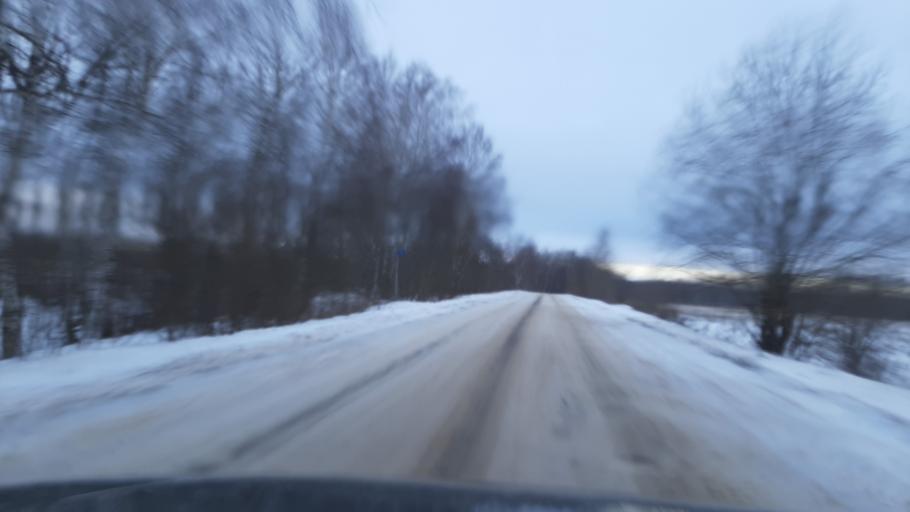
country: RU
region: Kostroma
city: Volgorechensk
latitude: 57.4375
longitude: 41.0503
